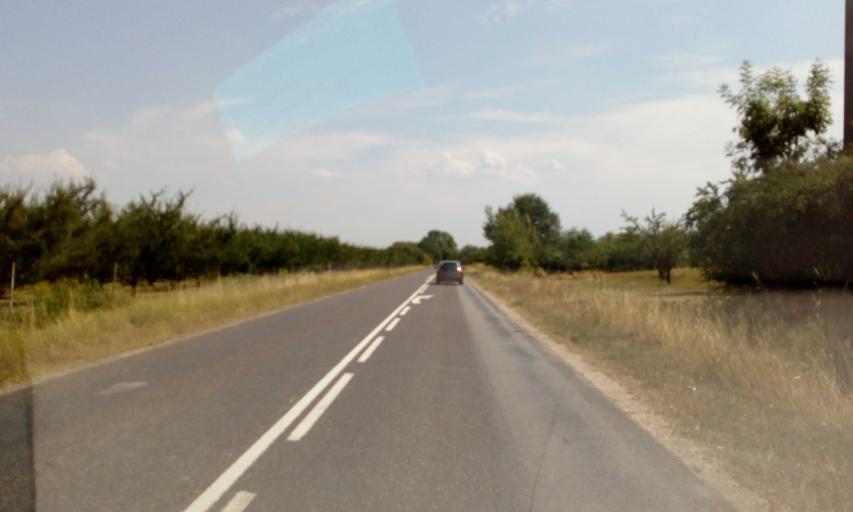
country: FR
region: Lorraine
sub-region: Departement de la Meuse
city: Vigneulles-les-Hattonchatel
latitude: 48.9979
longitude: 5.7075
